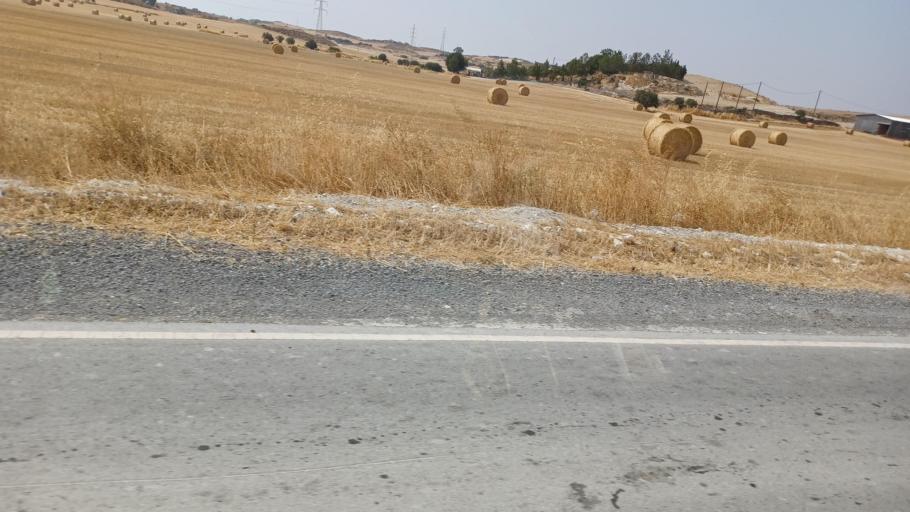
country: CY
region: Larnaka
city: Aradippou
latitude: 34.9370
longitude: 33.5499
